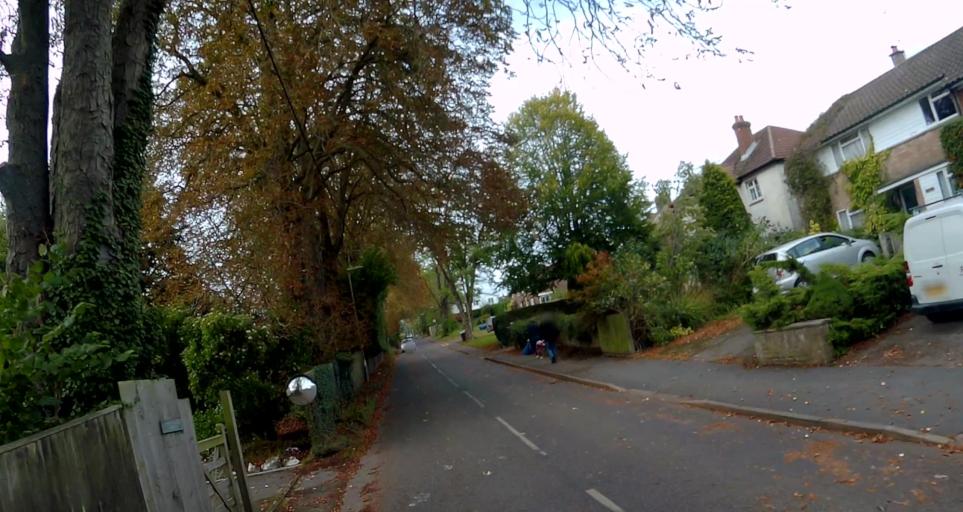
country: GB
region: England
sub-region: Hampshire
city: Kings Worthy
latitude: 51.0831
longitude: -1.1754
